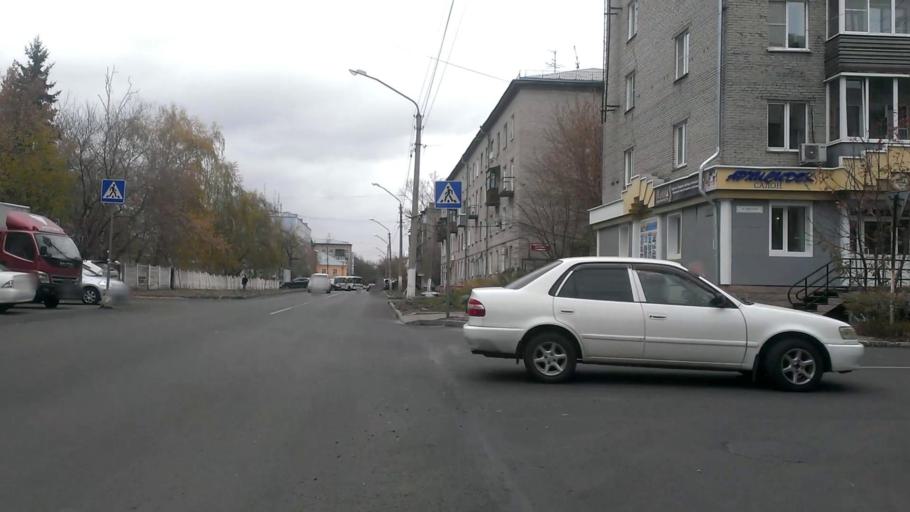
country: RU
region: Altai Krai
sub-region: Gorod Barnaulskiy
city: Barnaul
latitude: 53.3512
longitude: 83.7695
